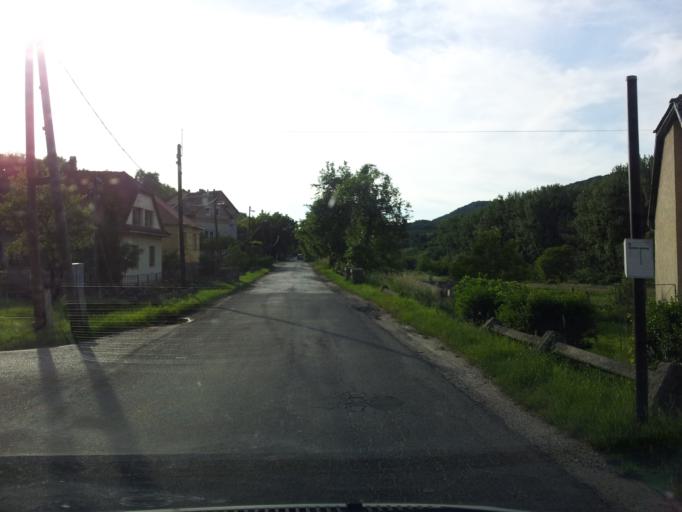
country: HU
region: Komarom-Esztergom
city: Kesztolc
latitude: 47.7302
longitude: 18.8413
